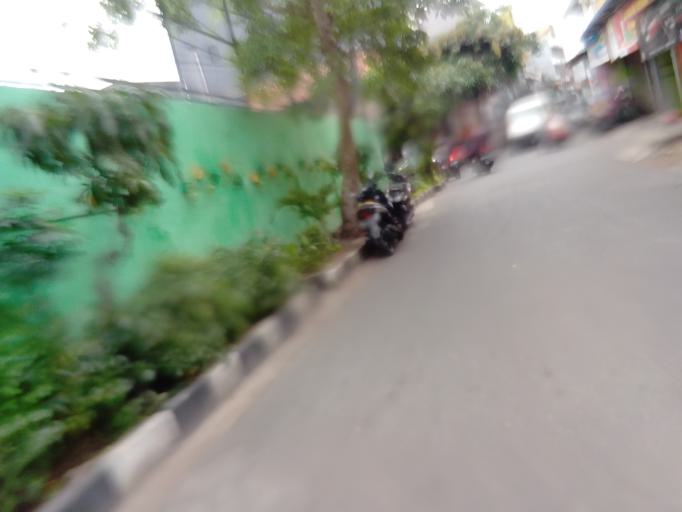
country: ID
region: Jakarta Raya
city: Jakarta
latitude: -6.1543
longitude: 106.8135
